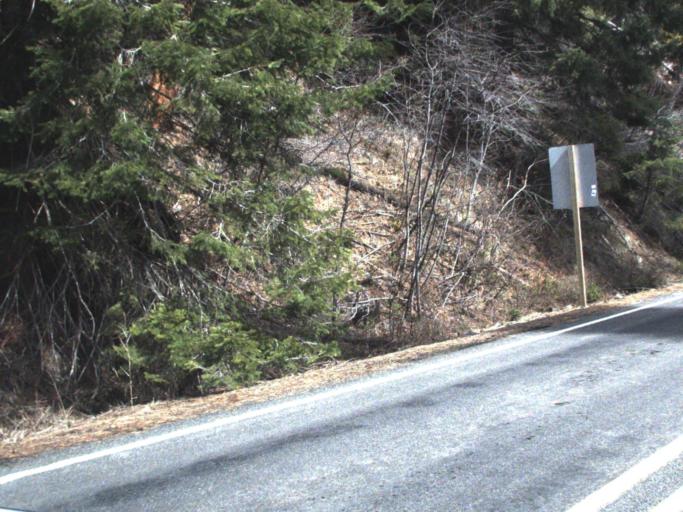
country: US
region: Washington
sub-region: Kittitas County
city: Cle Elum
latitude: 46.9781
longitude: -121.1683
